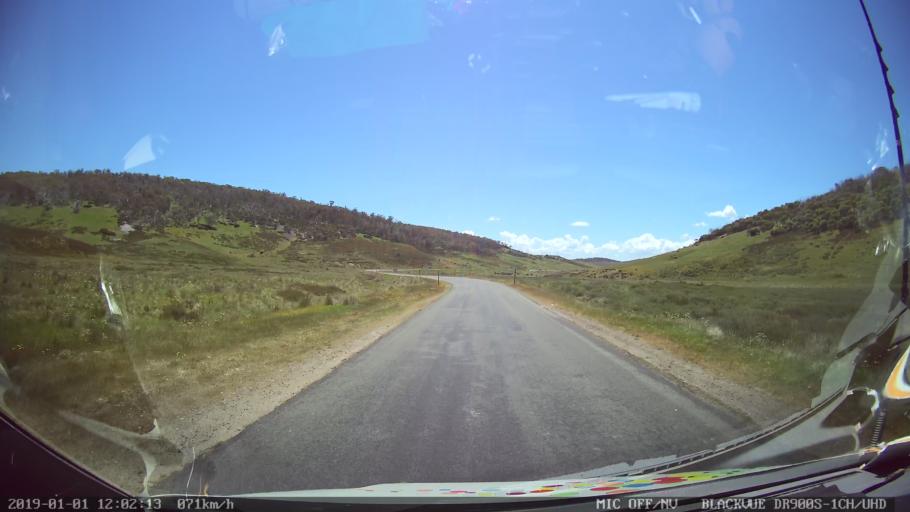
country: AU
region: New South Wales
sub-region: Snowy River
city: Jindabyne
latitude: -35.8741
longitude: 148.4747
